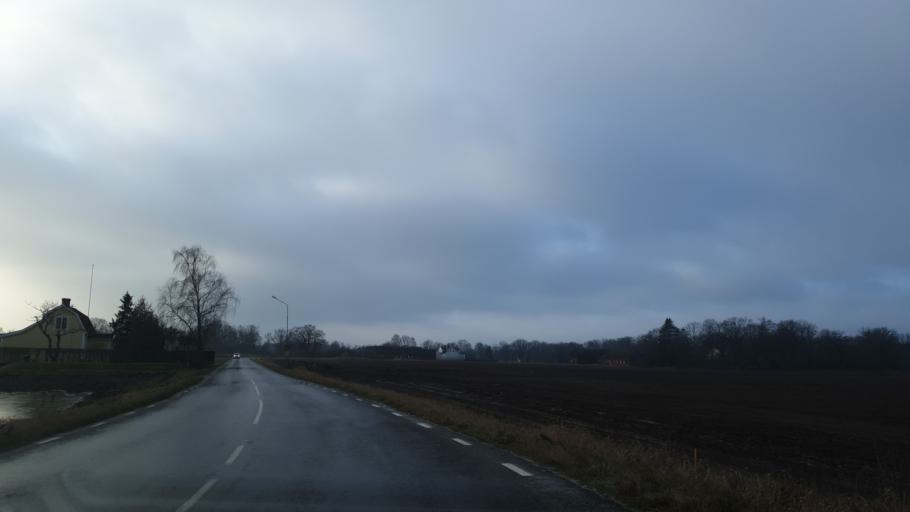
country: SE
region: Blekinge
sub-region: Karlshamns Kommun
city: Morrum
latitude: 56.1664
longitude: 14.7586
